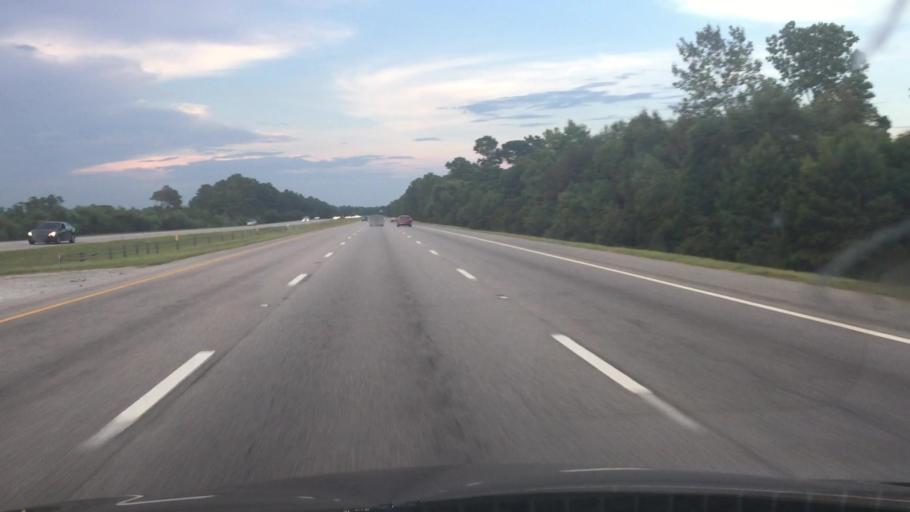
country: US
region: South Carolina
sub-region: Horry County
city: Myrtle Beach
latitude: 33.7741
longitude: -78.8178
